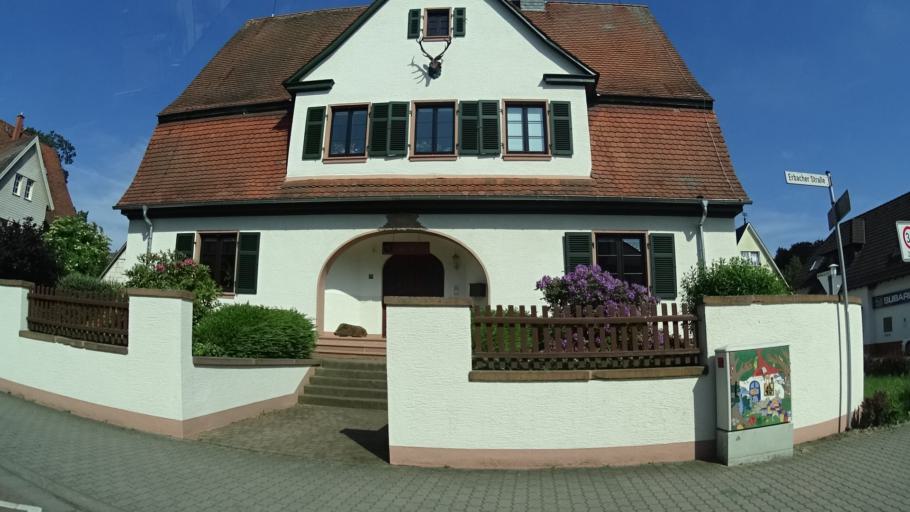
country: DE
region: Hesse
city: Michelstadt
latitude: 49.6748
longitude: 9.0048
